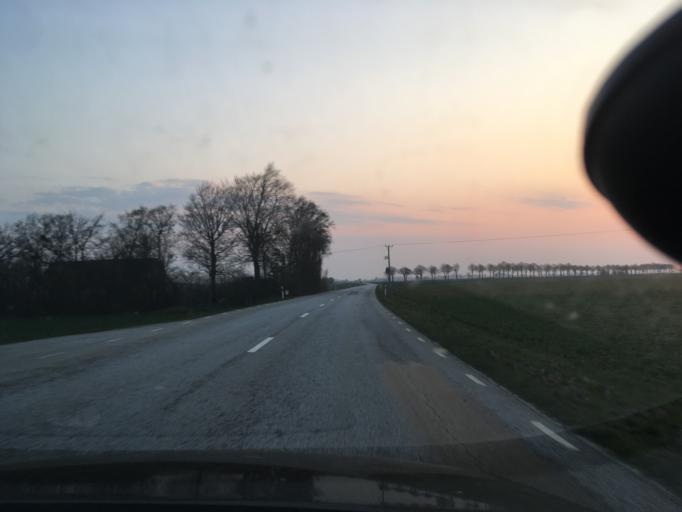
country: SE
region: Skane
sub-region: Ystads Kommun
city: Kopingebro
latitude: 55.4685
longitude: 14.0426
